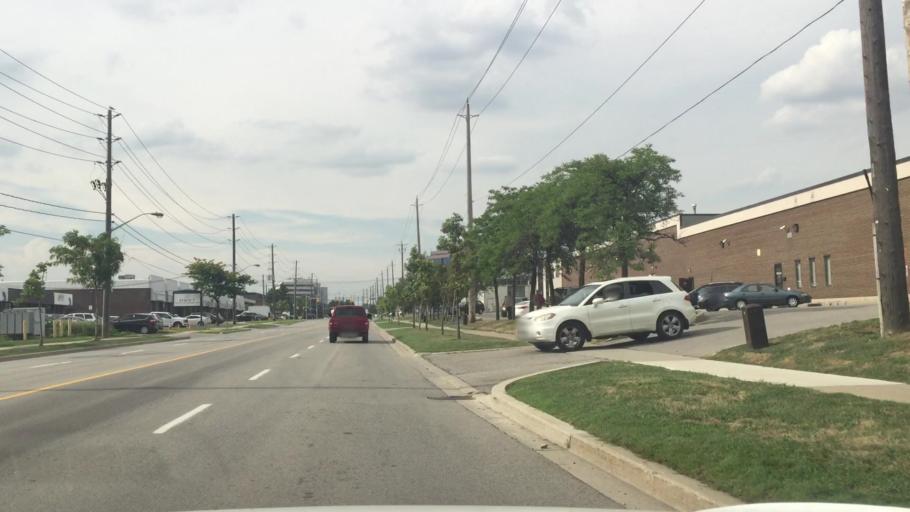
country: CA
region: Ontario
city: Concord
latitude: 43.7661
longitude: -79.5412
